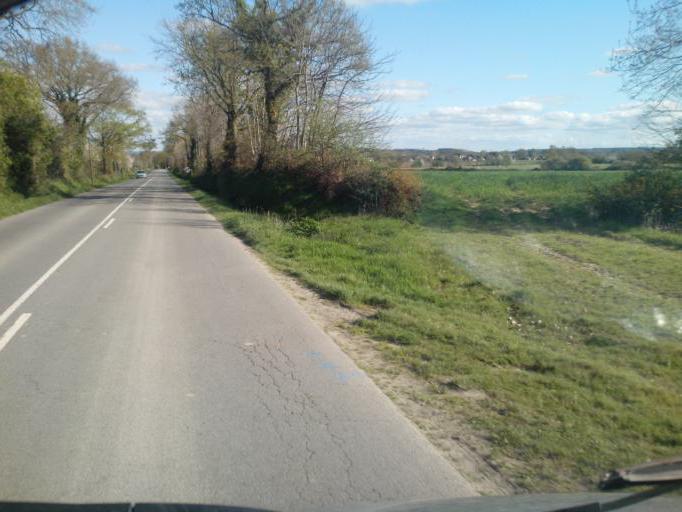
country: FR
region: Brittany
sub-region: Departement d'Ille-et-Vilaine
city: Guipry
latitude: 47.8514
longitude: -1.8743
